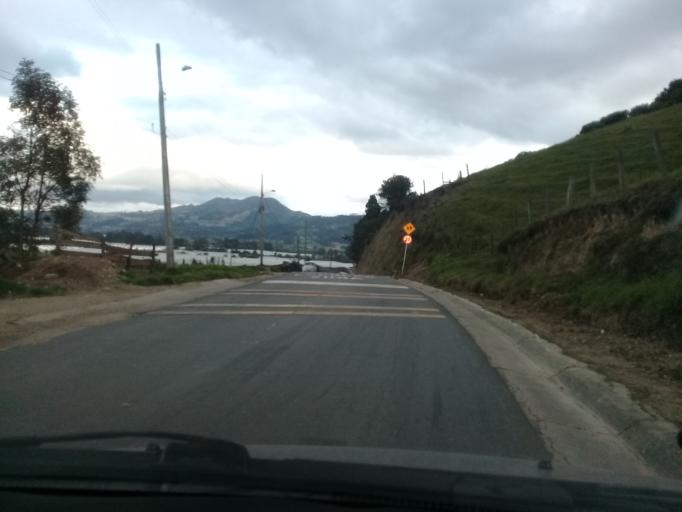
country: CO
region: Cundinamarca
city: Tabio
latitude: 4.9325
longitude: -74.1048
